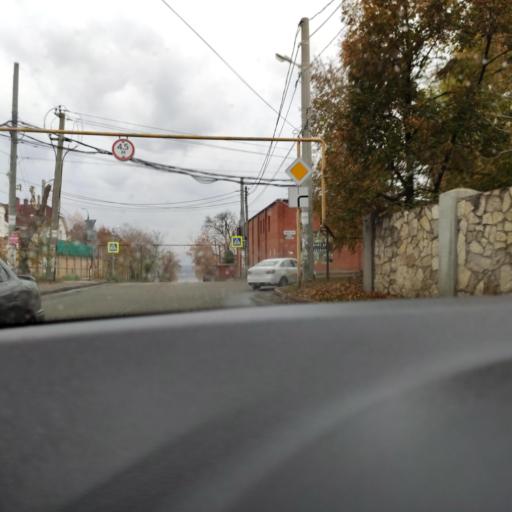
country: RU
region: Samara
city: Samara
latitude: 53.2758
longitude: 50.1909
